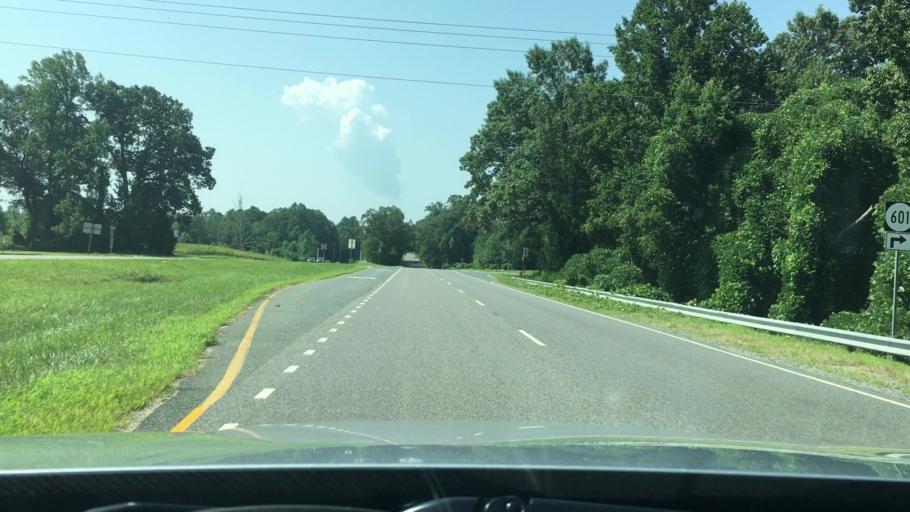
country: US
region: Virginia
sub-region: Caroline County
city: Bowling Green
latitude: 37.9996
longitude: -77.4163
